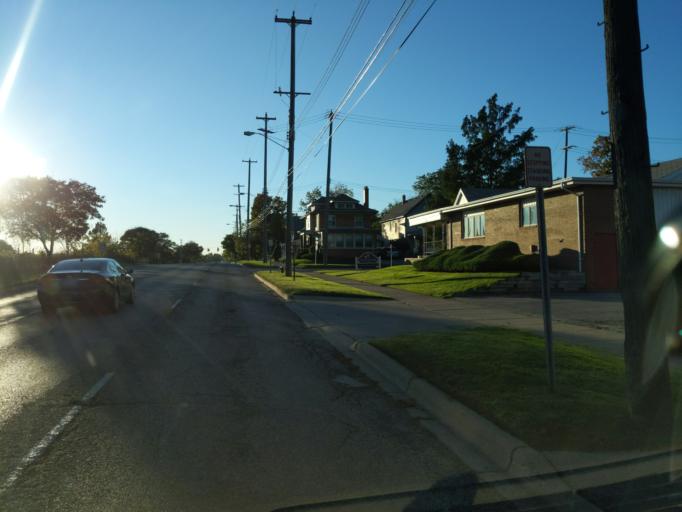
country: US
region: Michigan
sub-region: Ingham County
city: Lansing
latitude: 42.7265
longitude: -84.5579
